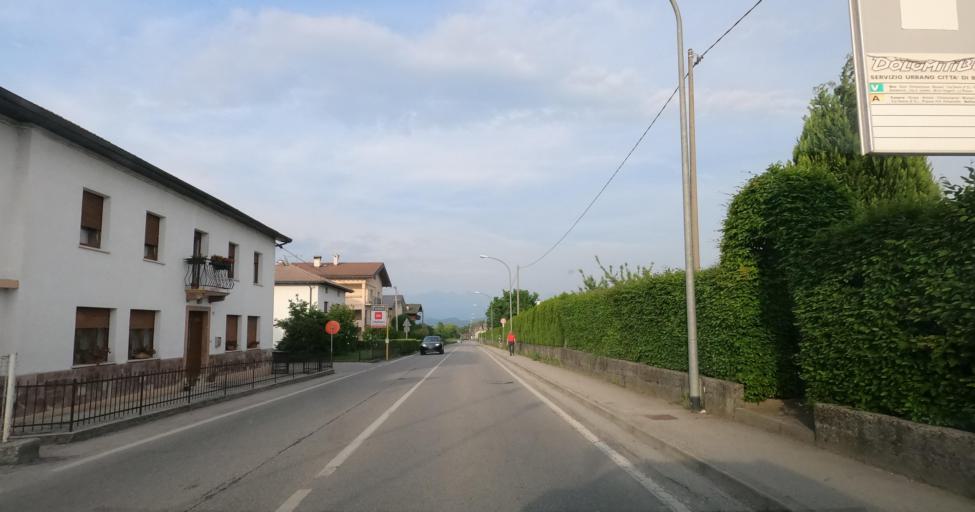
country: IT
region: Veneto
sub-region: Provincia di Belluno
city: Belluno
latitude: 46.1408
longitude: 12.1840
